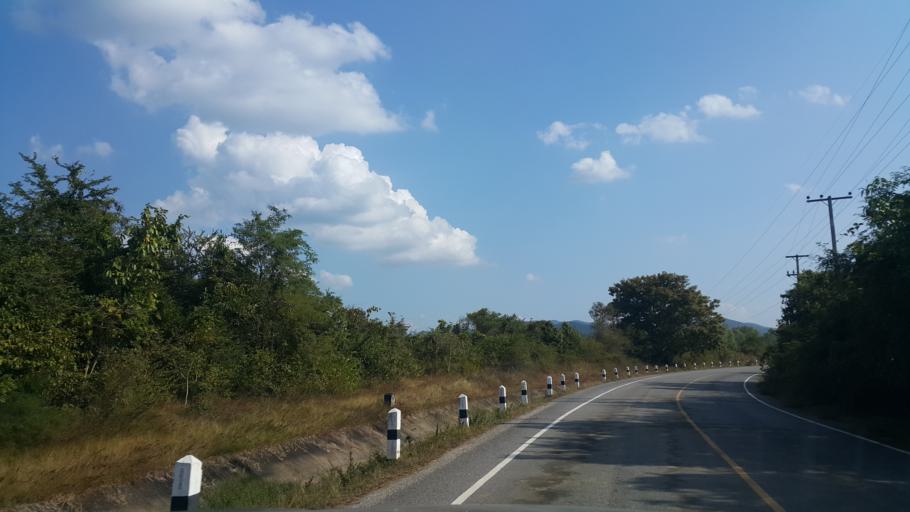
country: TH
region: Lamphun
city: Mae Tha
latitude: 18.5346
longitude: 99.0970
